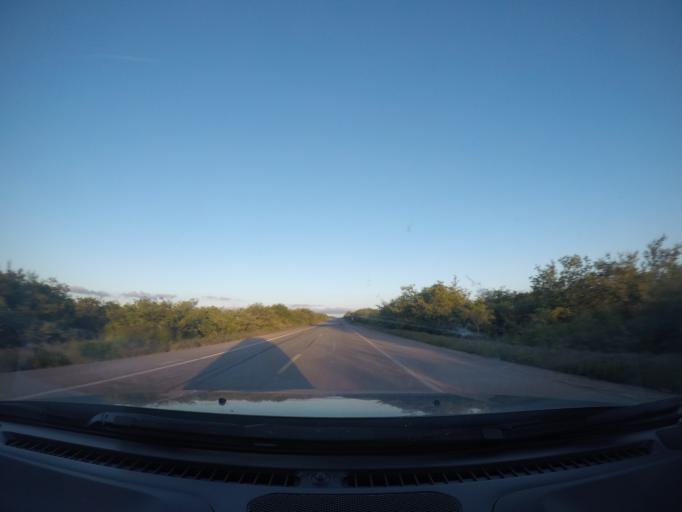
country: BR
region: Bahia
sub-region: Seabra
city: Seabra
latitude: -12.3911
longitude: -41.9073
